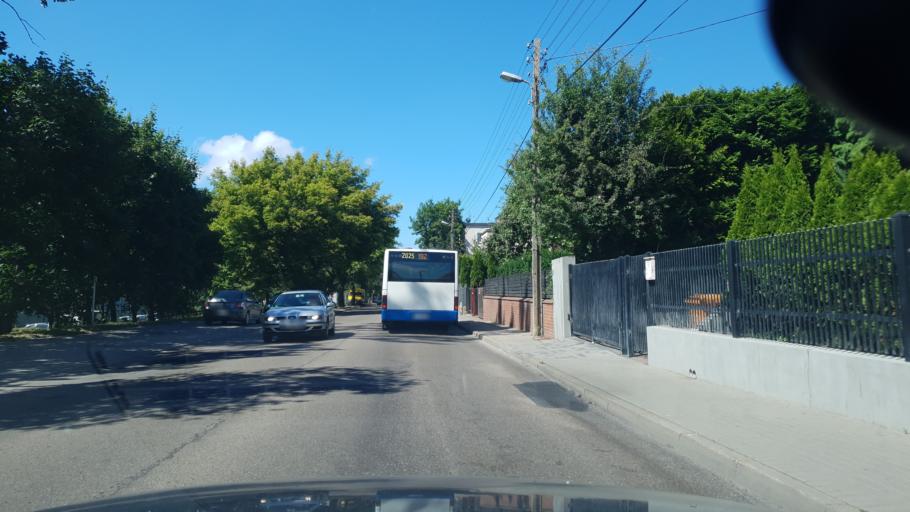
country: PL
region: Pomeranian Voivodeship
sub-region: Gdynia
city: Gdynia
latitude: 54.4997
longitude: 18.5417
